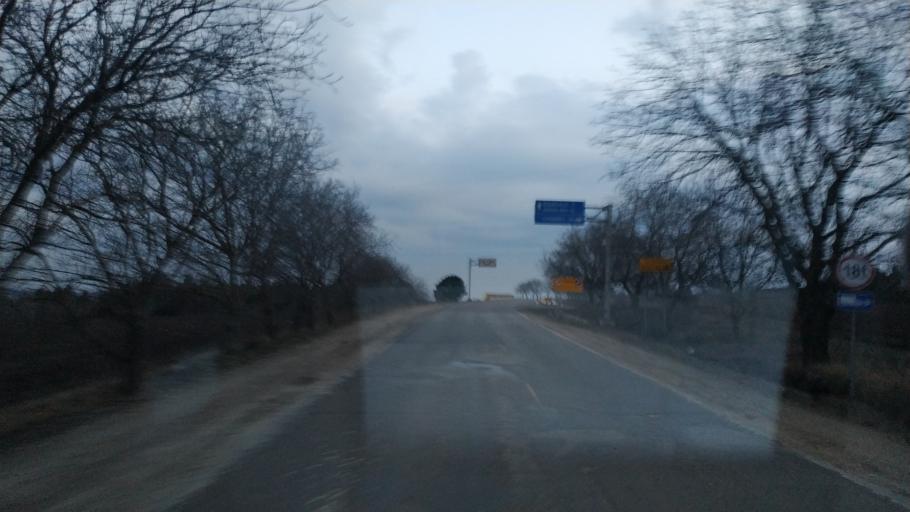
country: MD
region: Anenii Noi
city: Anenii Noi
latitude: 46.9292
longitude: 29.2872
